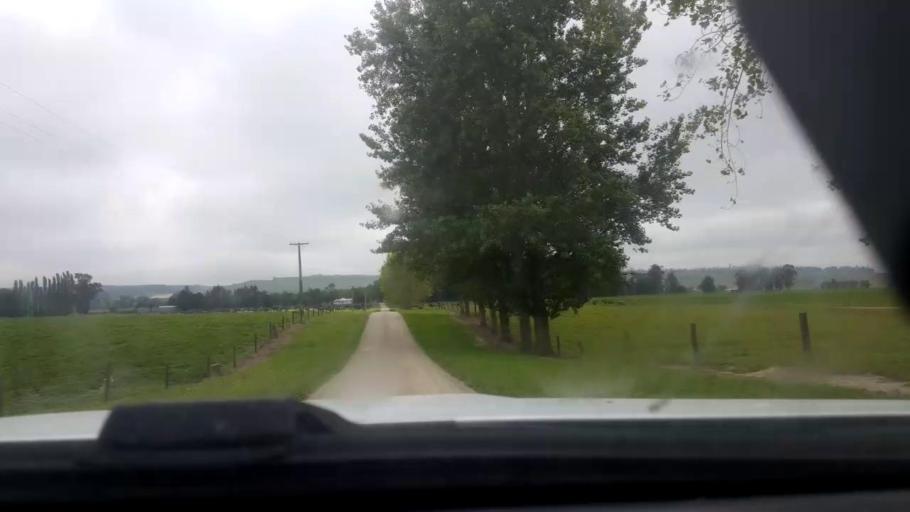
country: NZ
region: Canterbury
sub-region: Timaru District
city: Pleasant Point
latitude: -44.2116
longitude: 171.1097
